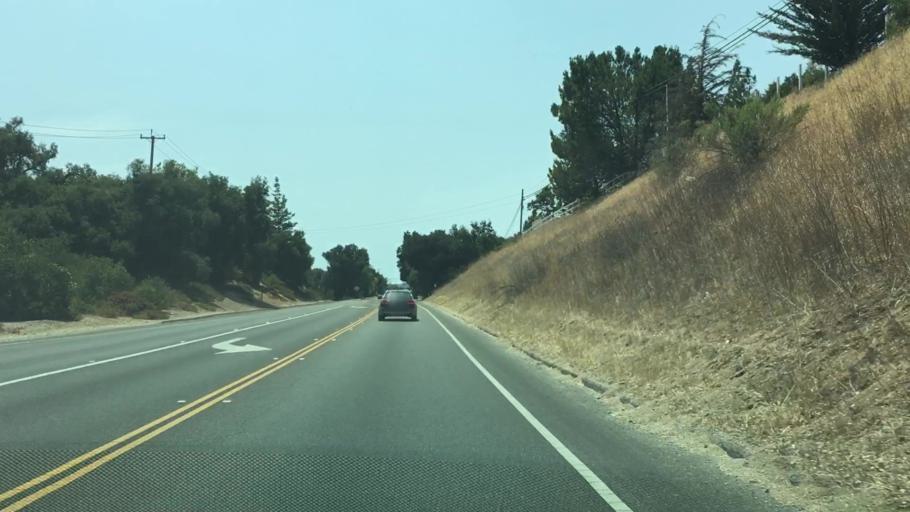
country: US
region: California
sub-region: Santa Barbara County
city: Santa Ynez
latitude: 34.6095
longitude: -120.0880
